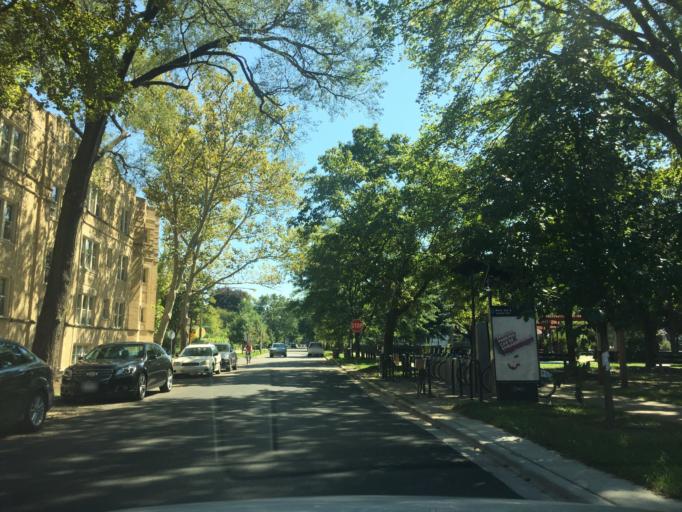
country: US
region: Illinois
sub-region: Cook County
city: Lincolnwood
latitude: 41.9661
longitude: -87.7009
